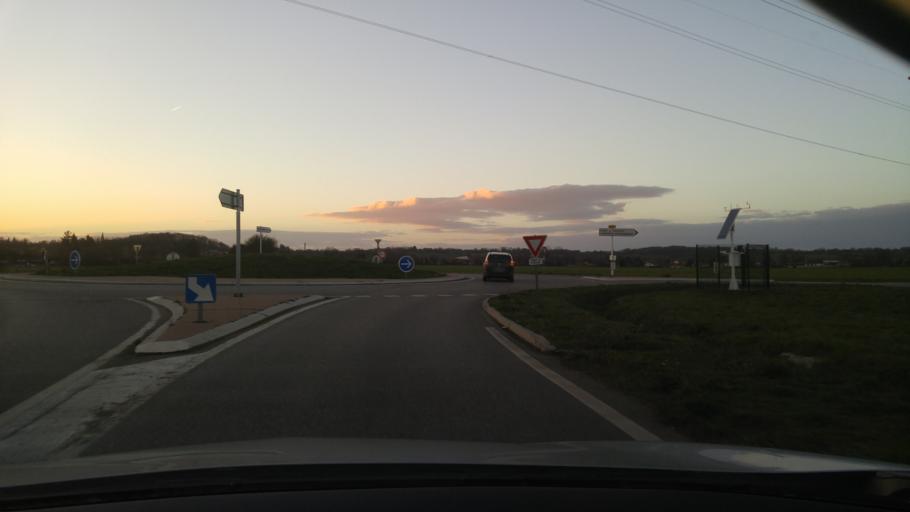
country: FR
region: Rhone-Alpes
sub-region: Departement de l'Isere
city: Satolas-et-Bonce
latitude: 45.7141
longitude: 5.1386
